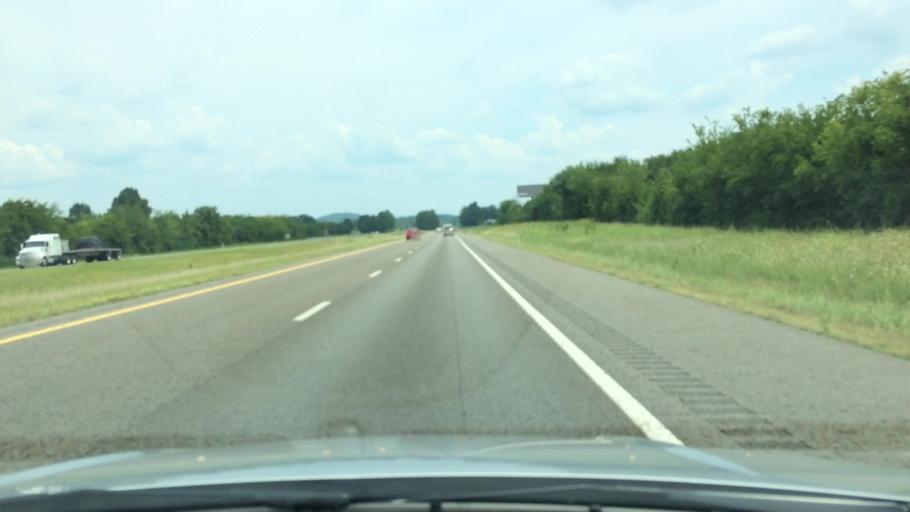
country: US
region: Tennessee
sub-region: Marshall County
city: Cornersville
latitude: 35.4368
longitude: -86.8811
